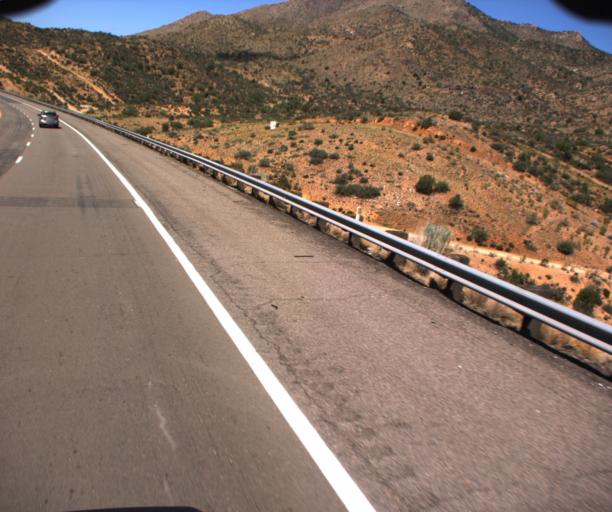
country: US
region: Arizona
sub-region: Mohave County
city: Peach Springs
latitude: 35.1716
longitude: -113.5196
